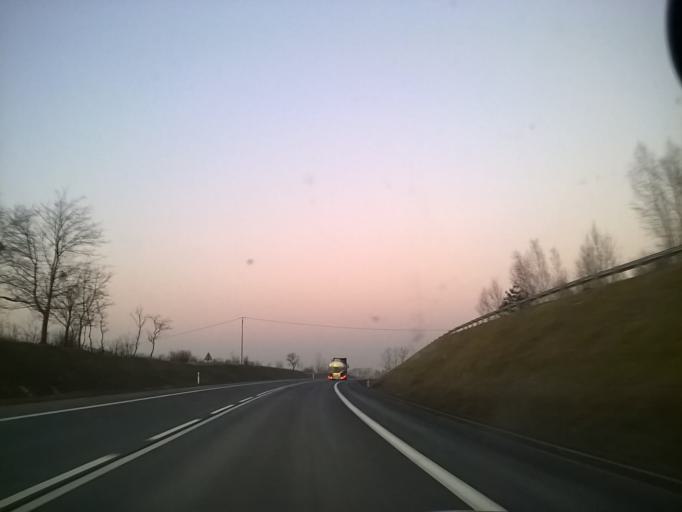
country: PL
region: Warmian-Masurian Voivodeship
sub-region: Powiat olsztynski
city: Barczewo
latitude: 53.8335
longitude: 20.6815
